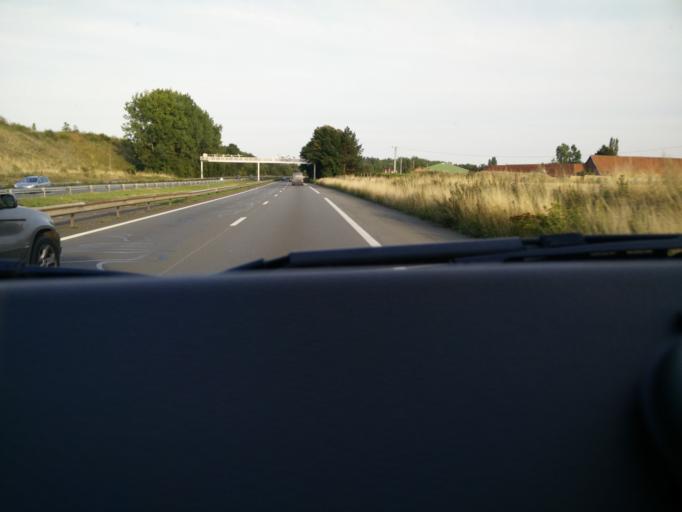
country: FR
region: Nord-Pas-de-Calais
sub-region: Departement du Nord
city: Sainghin-en-Melantois
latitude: 50.5639
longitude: 3.1648
